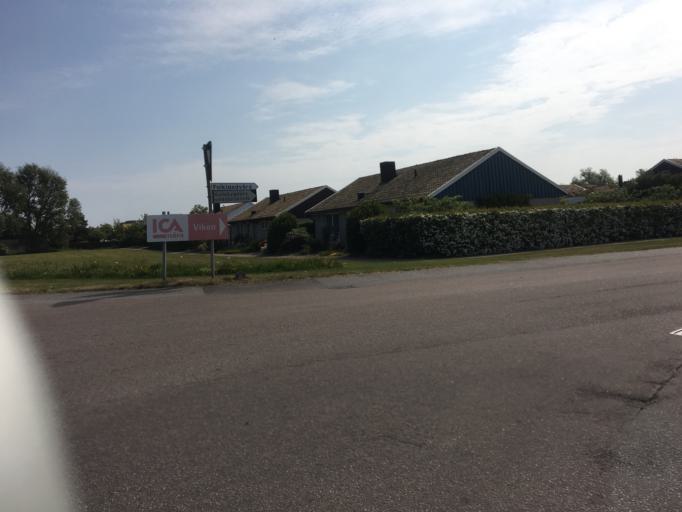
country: SE
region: Skane
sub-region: Hoganas Kommun
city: Hoganas
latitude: 56.1532
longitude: 12.5747
